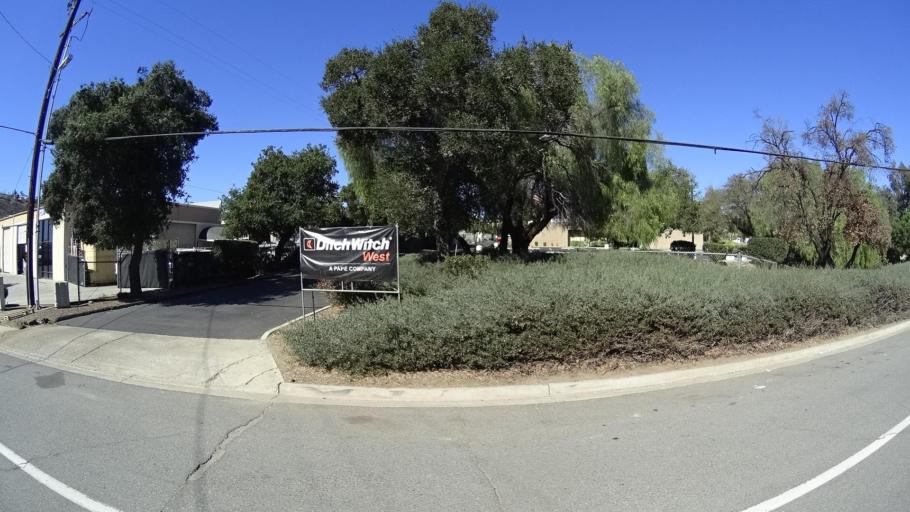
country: US
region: California
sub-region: San Diego County
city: Crest
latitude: 32.8476
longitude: -116.8697
